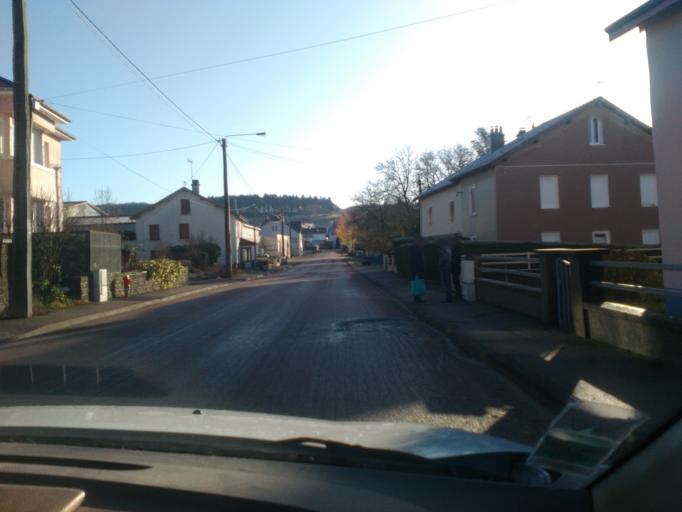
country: FR
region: Lorraine
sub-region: Departement des Vosges
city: Xertigny
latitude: 48.0479
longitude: 6.3985
